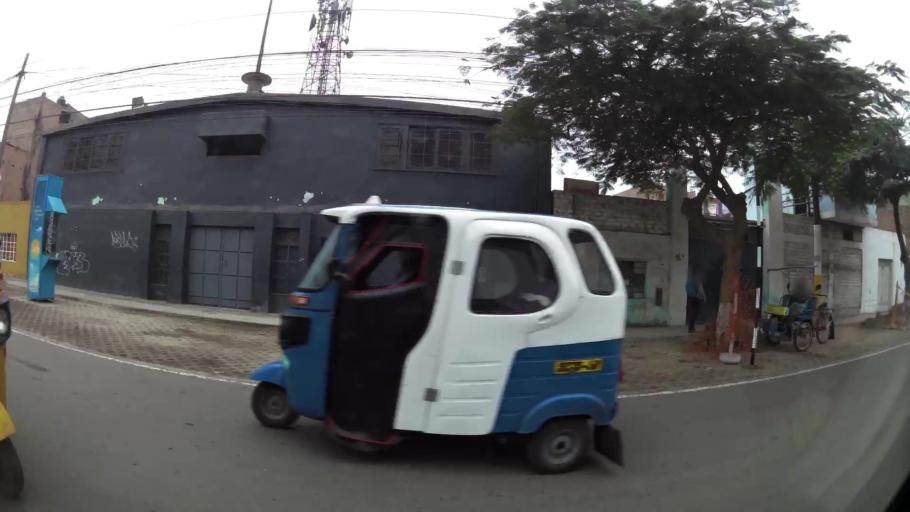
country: PE
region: Lima
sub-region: Lima
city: Carabayllo
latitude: -11.8674
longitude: -77.0762
